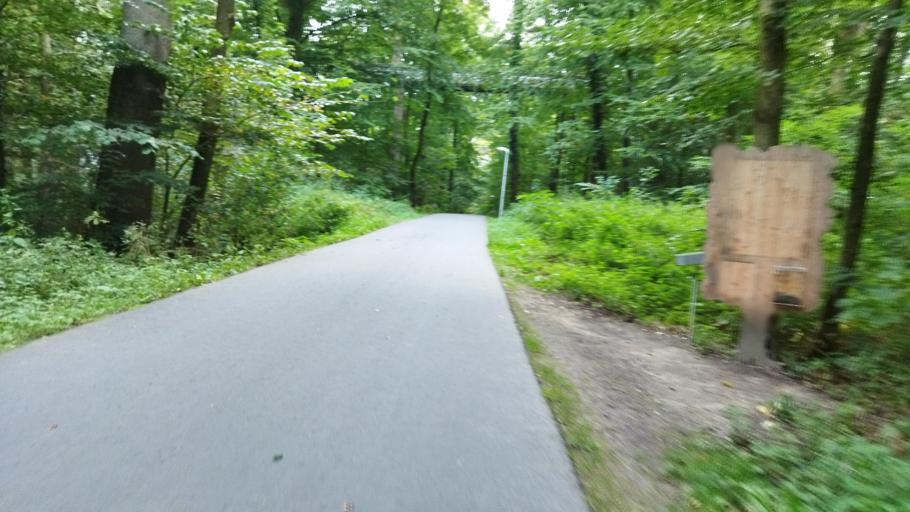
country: DE
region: Lower Saxony
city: Bad Iburg
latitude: 52.1630
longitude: 8.0329
